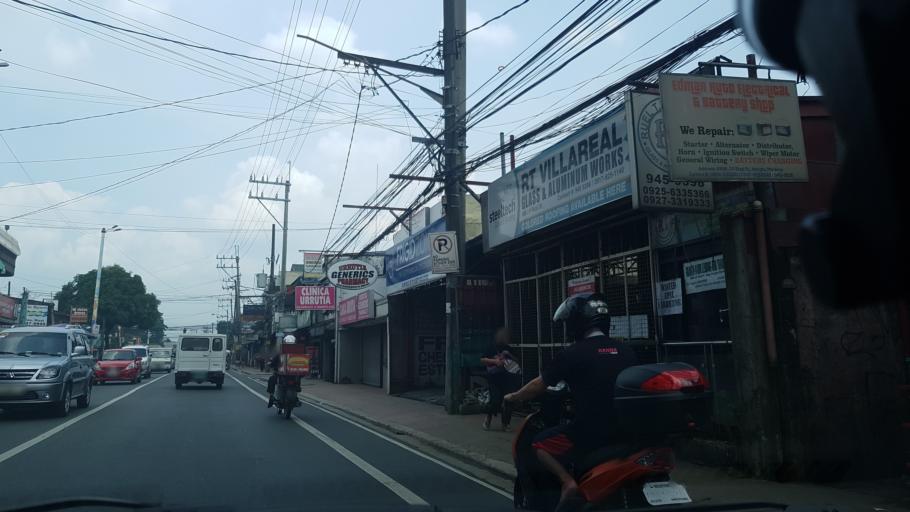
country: PH
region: Calabarzon
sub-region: Province of Rizal
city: San Mateo
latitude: 14.6715
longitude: 121.1089
